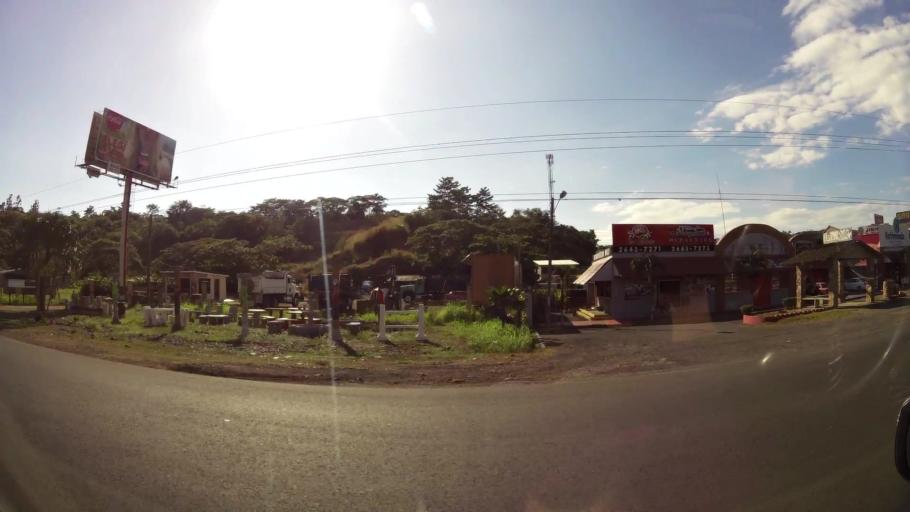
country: CR
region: Puntarenas
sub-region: Canton de Garabito
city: Jaco
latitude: 9.6436
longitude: -84.6277
